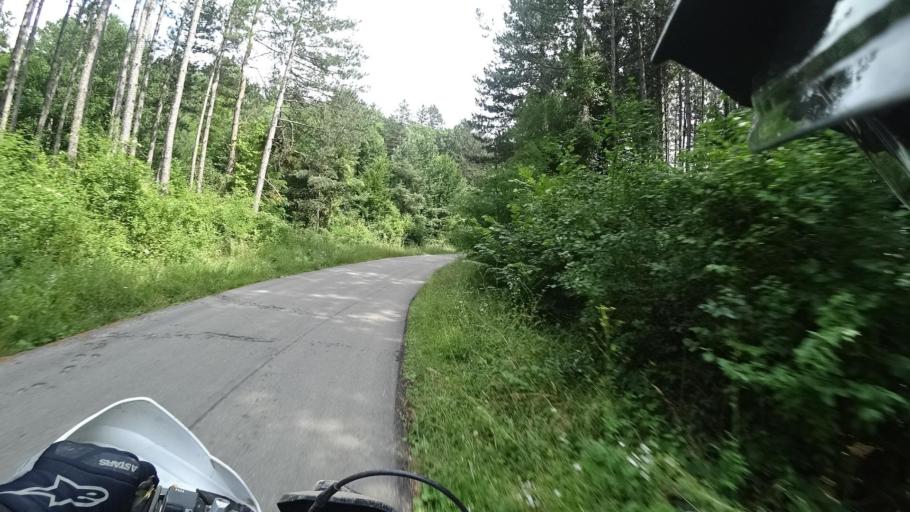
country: HR
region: Zadarska
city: Gracac
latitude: 44.5261
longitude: 15.7842
